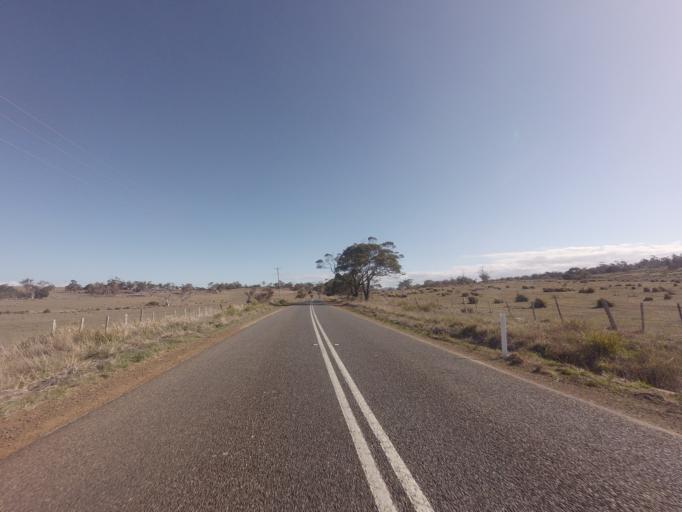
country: AU
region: Tasmania
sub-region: Sorell
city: Sorell
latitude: -42.2946
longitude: 147.9887
